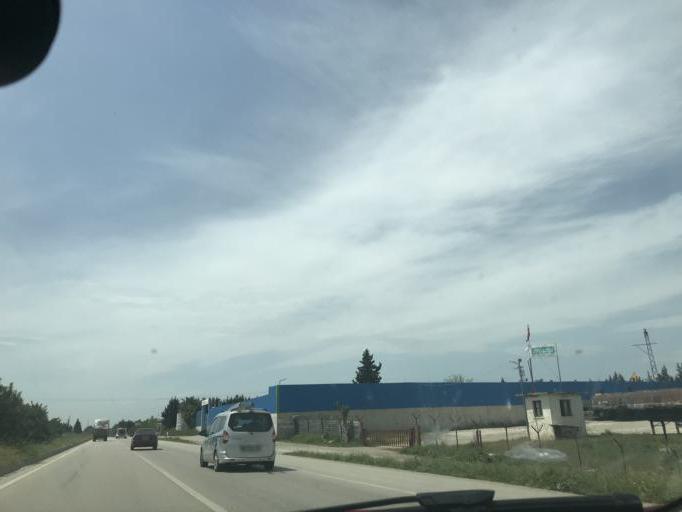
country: TR
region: Adana
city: Yakapinar
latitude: 36.9710
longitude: 35.5248
